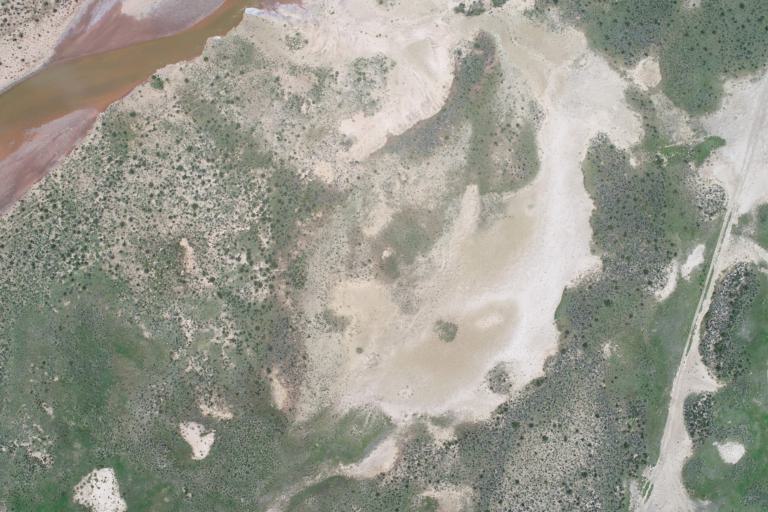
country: BO
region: La Paz
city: Curahuara de Carangas
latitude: -17.3203
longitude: -68.5158
